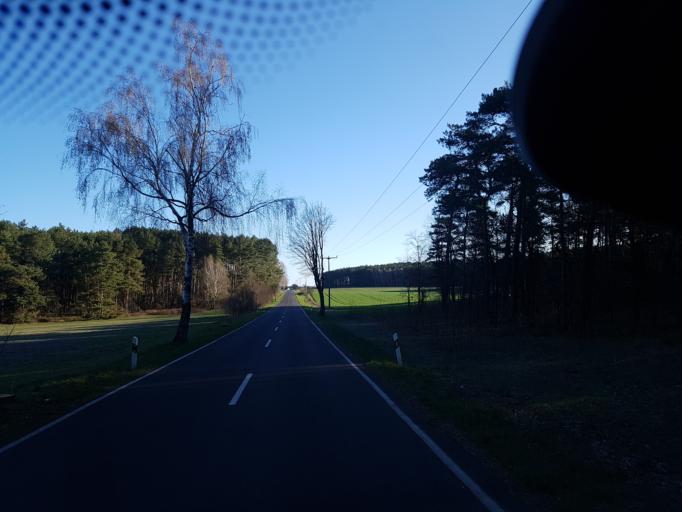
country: DE
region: Brandenburg
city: Jamlitz
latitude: 52.0521
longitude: 14.4272
